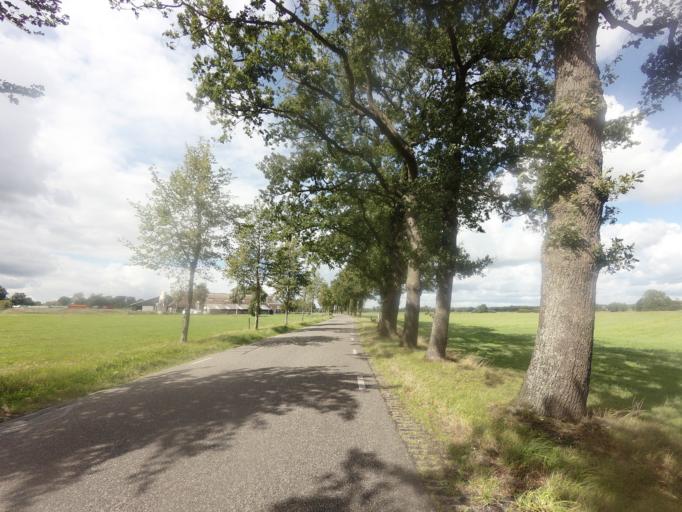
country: NL
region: Overijssel
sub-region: Gemeente Staphorst
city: Staphorst
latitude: 52.6760
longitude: 6.2365
